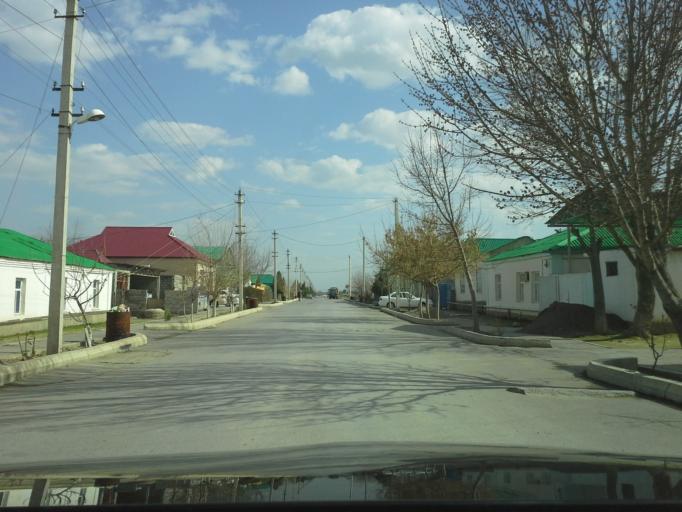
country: TM
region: Ahal
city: Ashgabat
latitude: 37.9866
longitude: 58.2816
